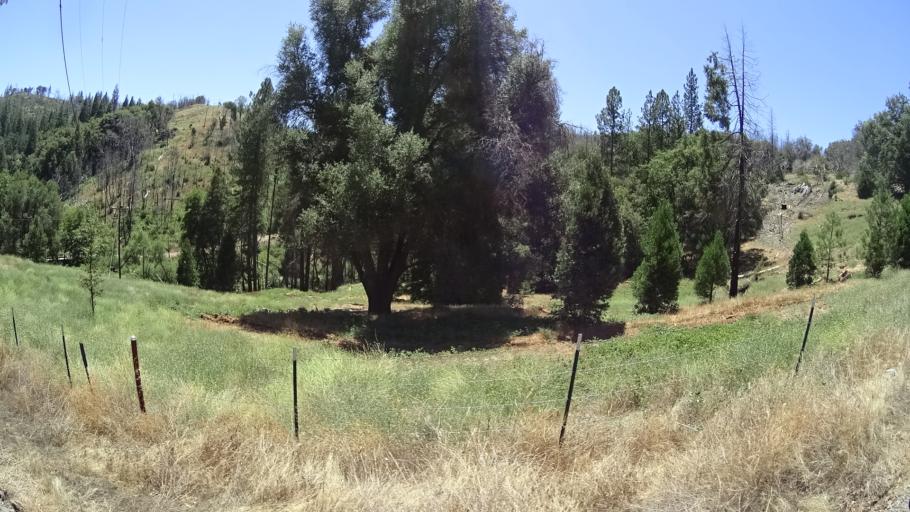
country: US
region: California
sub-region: Calaveras County
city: Mountain Ranch
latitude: 38.2590
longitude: -120.5799
